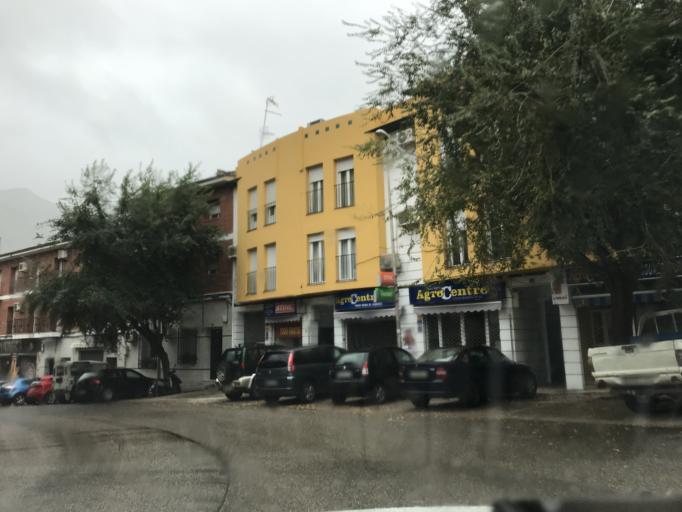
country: ES
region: Andalusia
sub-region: Provincia de Jaen
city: Cazorla
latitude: 37.9170
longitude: -3.0069
